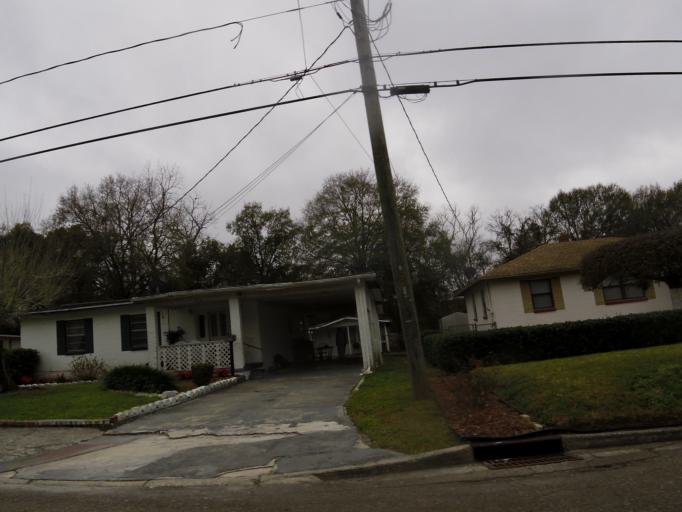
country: US
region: Florida
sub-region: Duval County
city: Jacksonville
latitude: 30.3703
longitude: -81.7140
